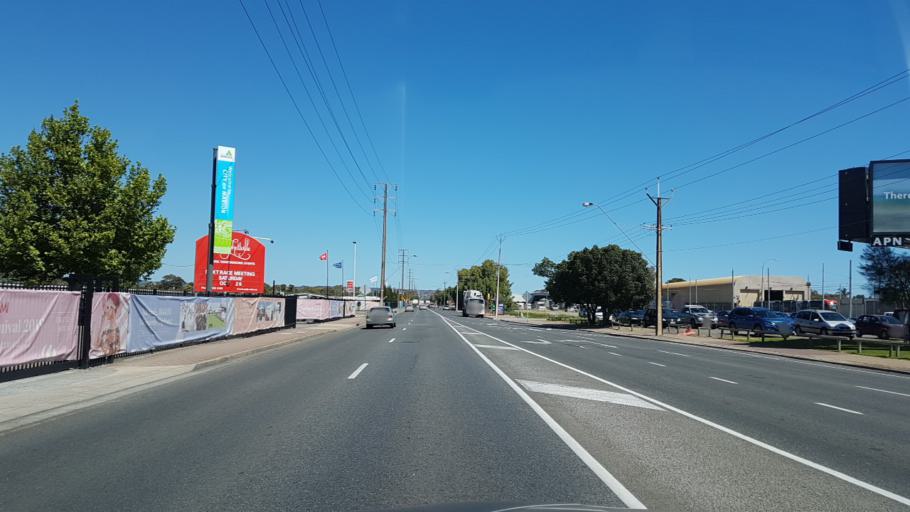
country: AU
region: South Australia
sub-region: Holdfast Bay
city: Glenelg East
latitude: -34.9764
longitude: 138.5379
